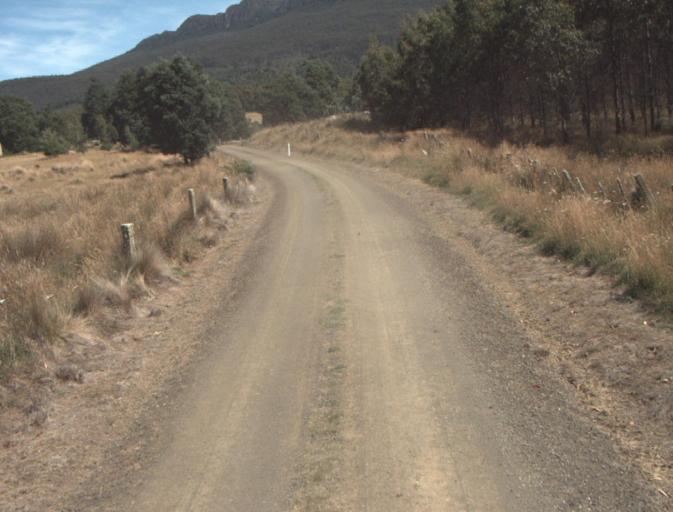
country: AU
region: Tasmania
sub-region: Dorset
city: Scottsdale
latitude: -41.3495
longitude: 147.4516
